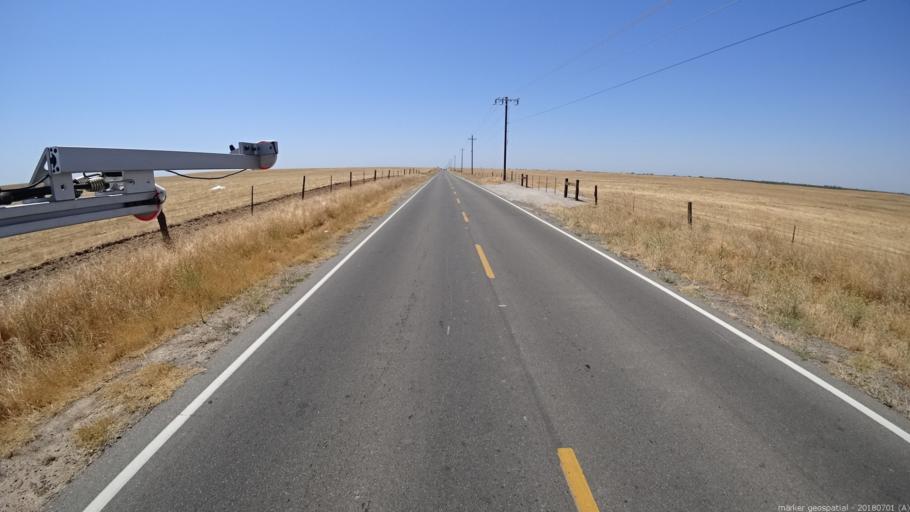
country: US
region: California
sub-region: Madera County
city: Madera Acres
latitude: 37.0196
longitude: -120.0289
